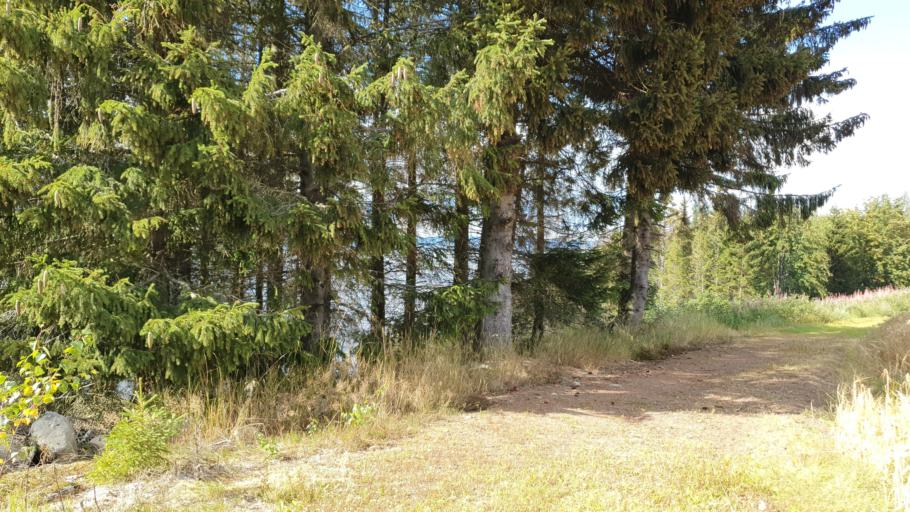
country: NO
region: Nord-Trondelag
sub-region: Levanger
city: Levanger
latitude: 63.7740
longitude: 11.3789
